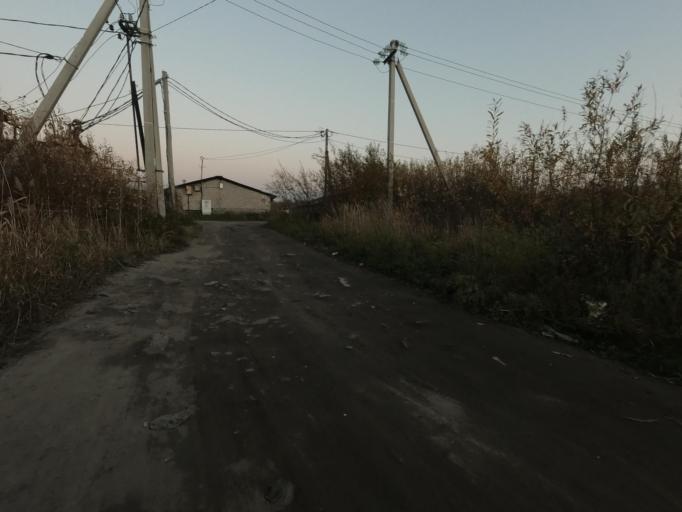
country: RU
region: Leningrad
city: Kirovsk
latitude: 59.8749
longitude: 31.0028
